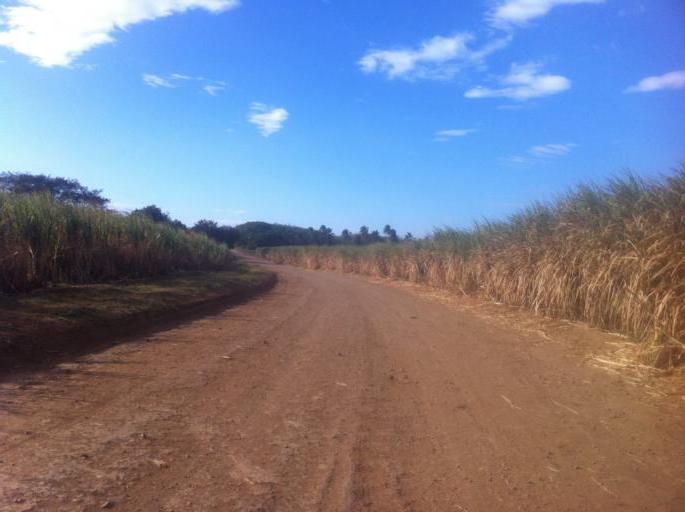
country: NI
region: Managua
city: Masachapa
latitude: 11.8350
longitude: -86.5145
